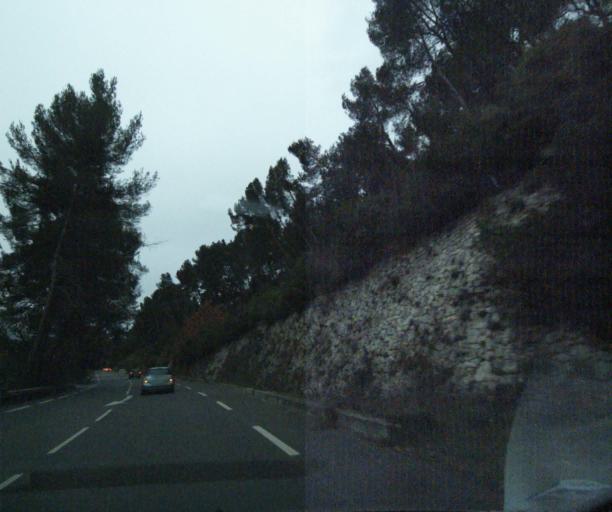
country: FR
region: Provence-Alpes-Cote d'Azur
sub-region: Departement des Bouches-du-Rhone
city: Aix-en-Provence
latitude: 43.5470
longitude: 5.4606
